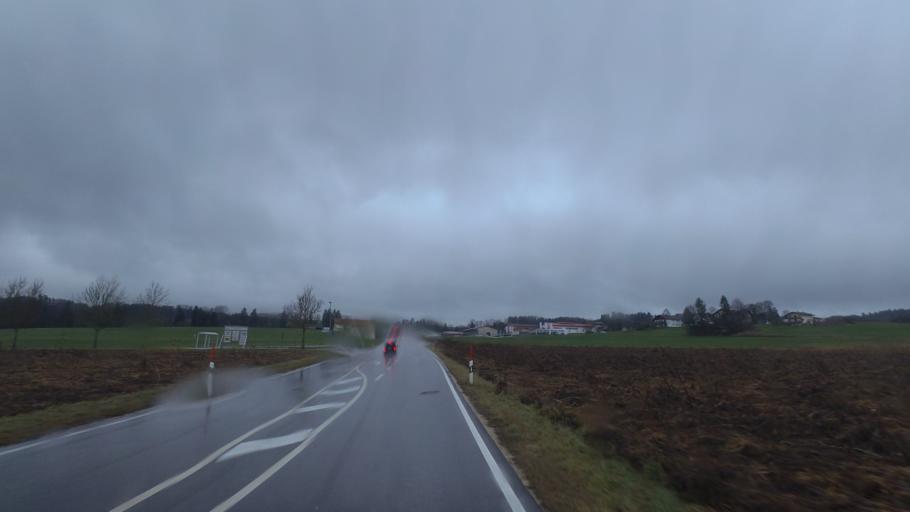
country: DE
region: Bavaria
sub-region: Upper Bavaria
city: Sankt Leonhard am Wonneberg
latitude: 47.9252
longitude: 12.7021
